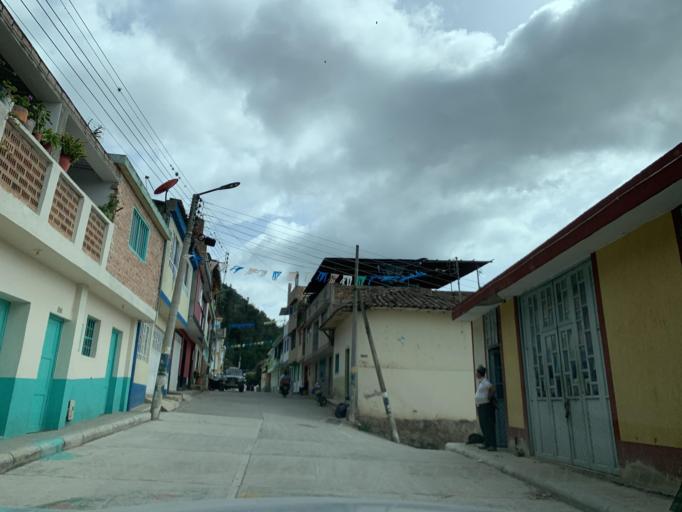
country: CO
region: Santander
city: Capitanejo
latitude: 6.5010
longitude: -72.7376
